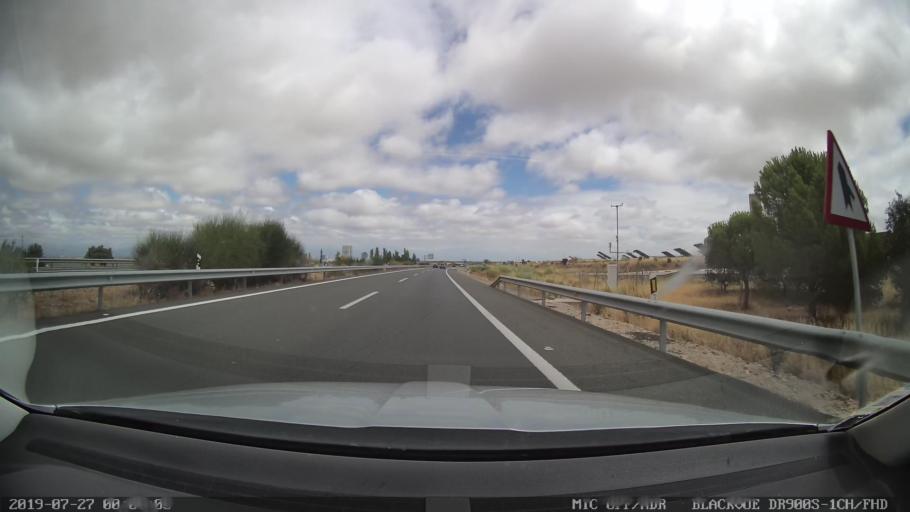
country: ES
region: Extremadura
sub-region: Provincia de Caceres
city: Almaraz
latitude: 39.8286
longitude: -5.6575
